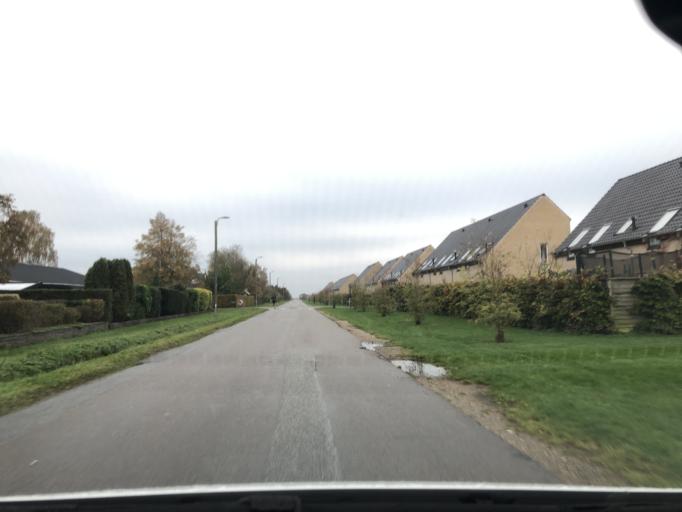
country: DK
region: Capital Region
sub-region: Dragor Kommune
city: Dragor
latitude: 55.5831
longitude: 12.6394
